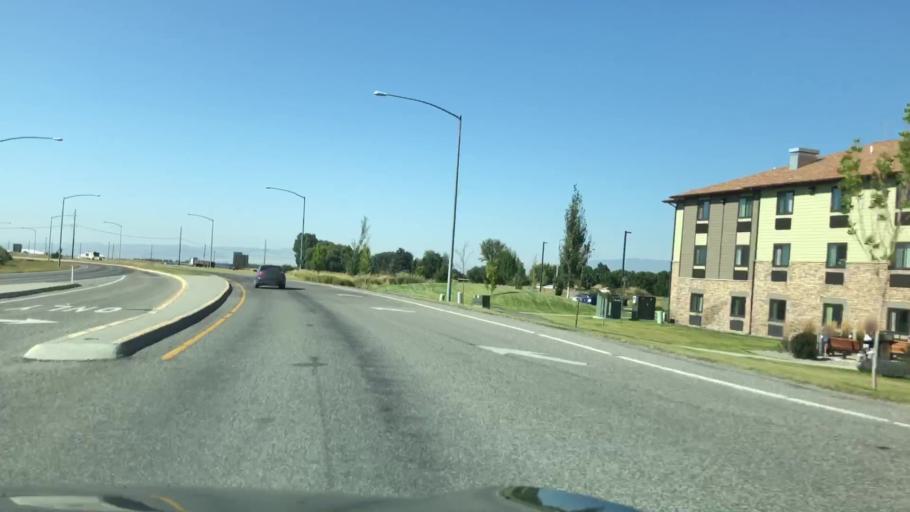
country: US
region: Montana
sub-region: Gallatin County
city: Bozeman
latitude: 45.7173
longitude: -111.0692
